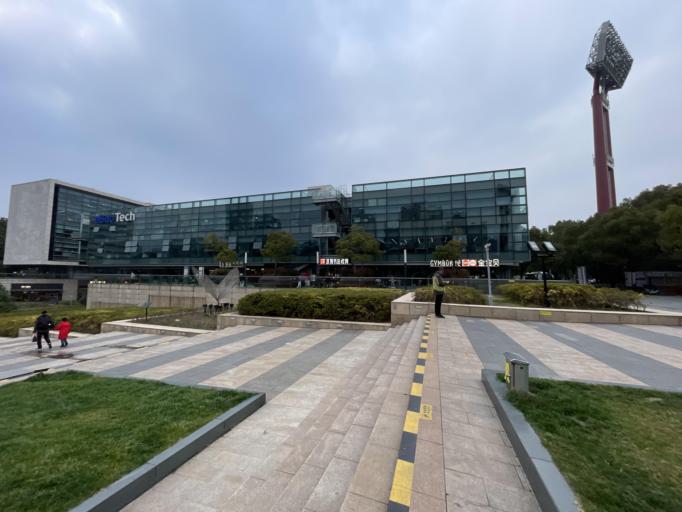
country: CN
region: Shanghai Shi
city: Yangpu
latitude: 31.3080
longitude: 121.5099
